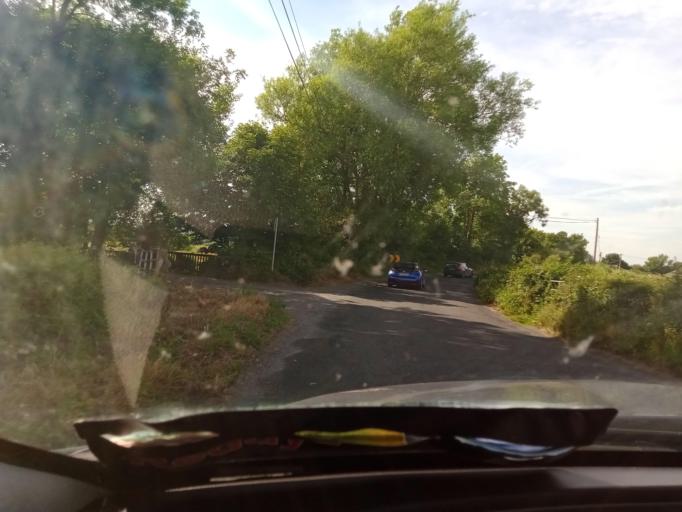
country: IE
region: Leinster
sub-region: Laois
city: Mountmellick
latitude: 53.1131
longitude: -7.3583
